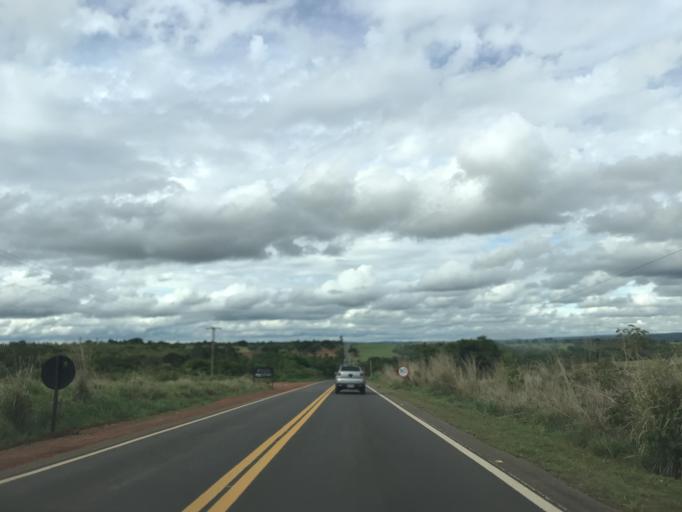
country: BR
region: Goias
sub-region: Piracanjuba
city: Piracanjuba
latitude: -17.1996
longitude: -48.7013
